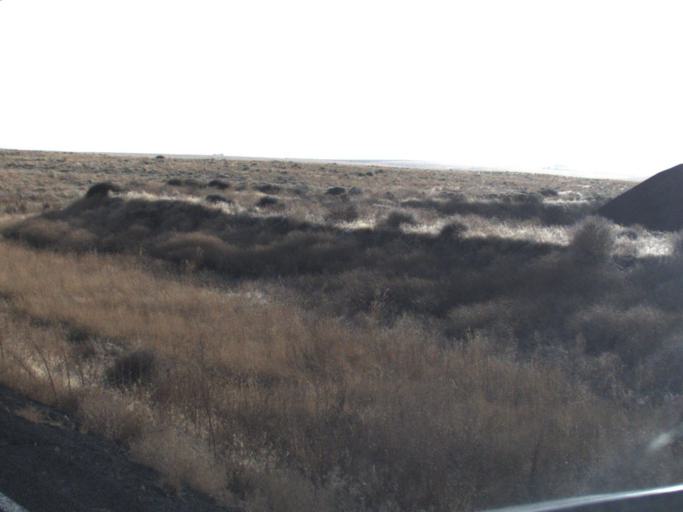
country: US
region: Washington
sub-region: Adams County
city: Ritzville
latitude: 47.3111
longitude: -118.6904
